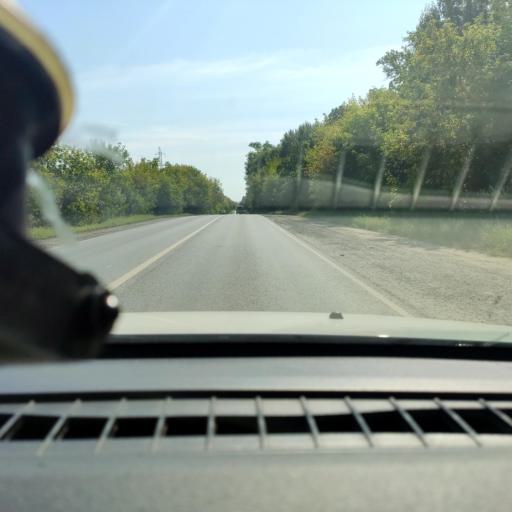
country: RU
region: Samara
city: Petra-Dubrava
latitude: 53.3180
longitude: 50.2686
